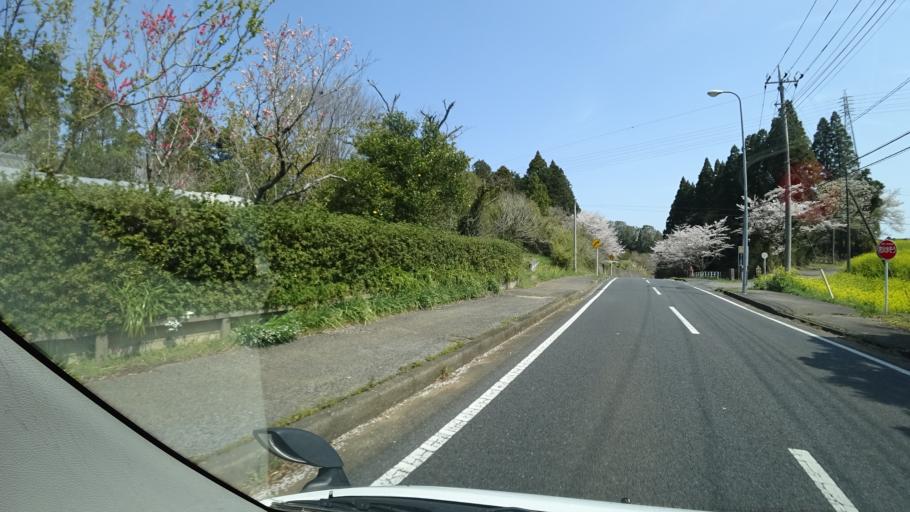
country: JP
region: Chiba
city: Naruto
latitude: 35.6939
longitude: 140.4232
